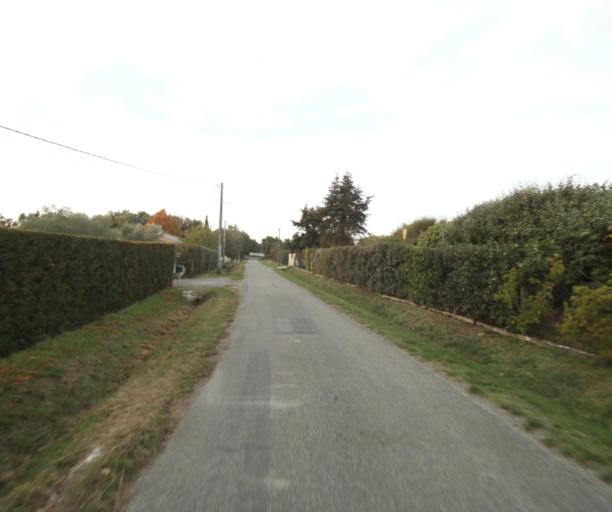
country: FR
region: Midi-Pyrenees
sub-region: Departement du Tarn-et-Garonne
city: Pompignan
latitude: 43.8247
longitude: 1.3144
